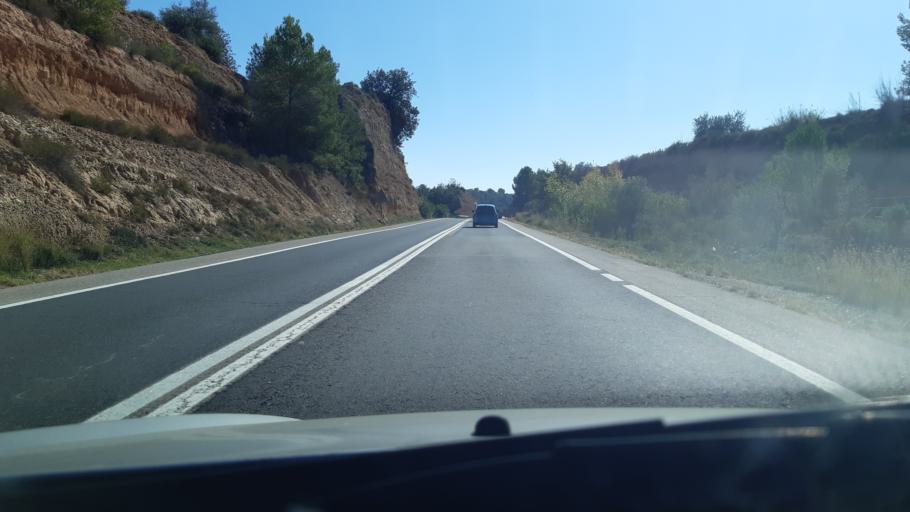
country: ES
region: Catalonia
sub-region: Provincia de Tarragona
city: Tivenys
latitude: 40.8886
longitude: 0.4911
